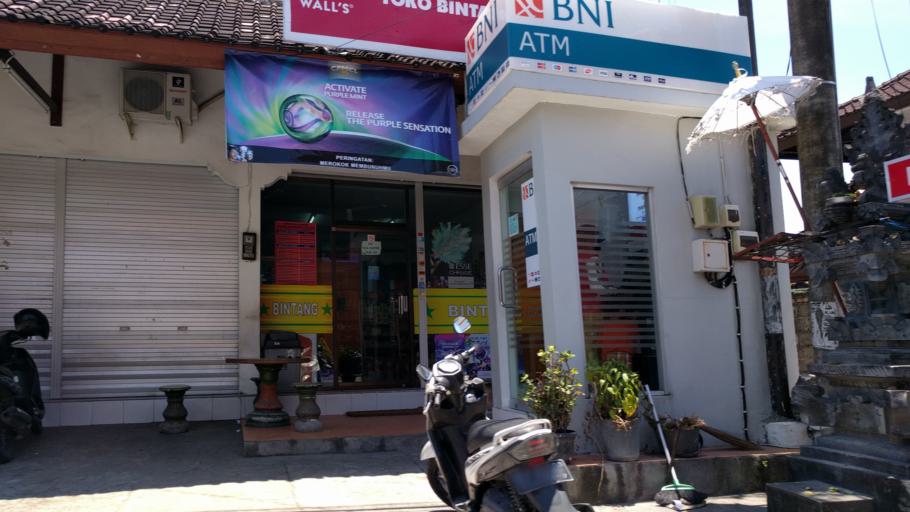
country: ID
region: Bali
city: Banjar Medura
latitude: -8.7056
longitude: 115.2529
